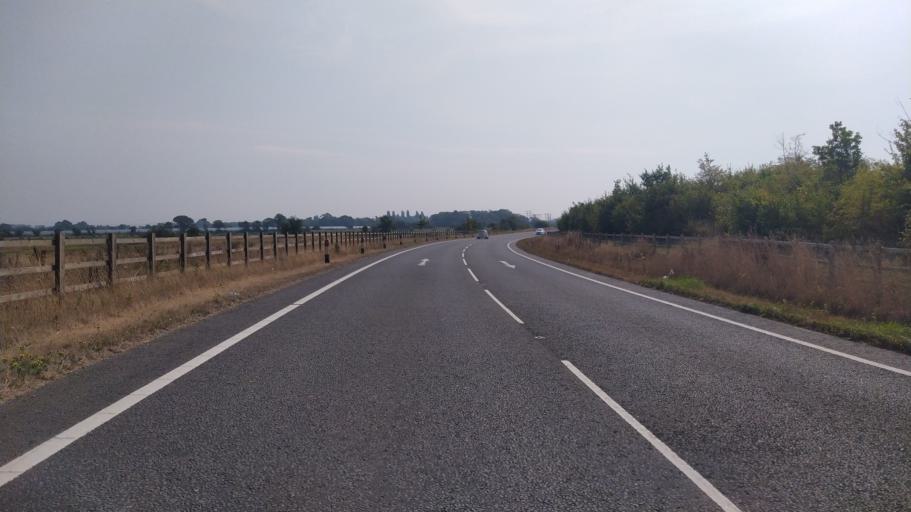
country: GB
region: England
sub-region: West Sussex
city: Bognor Regis
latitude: 50.8082
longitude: -0.6914
